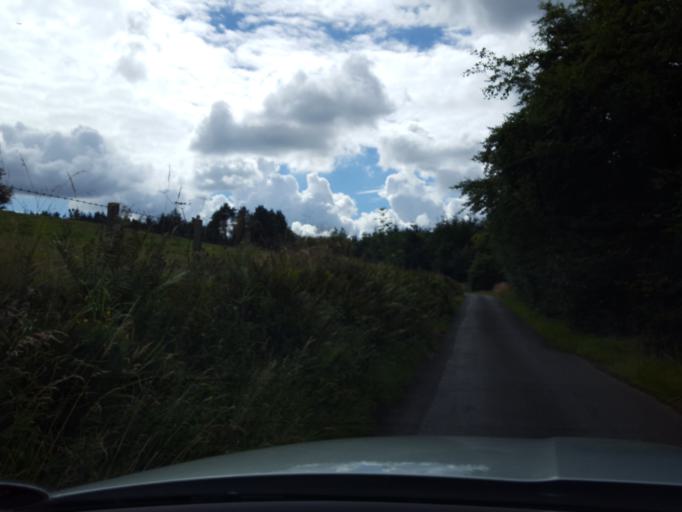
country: GB
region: Scotland
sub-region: West Lothian
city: Linlithgow
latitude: 55.9377
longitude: -3.6051
